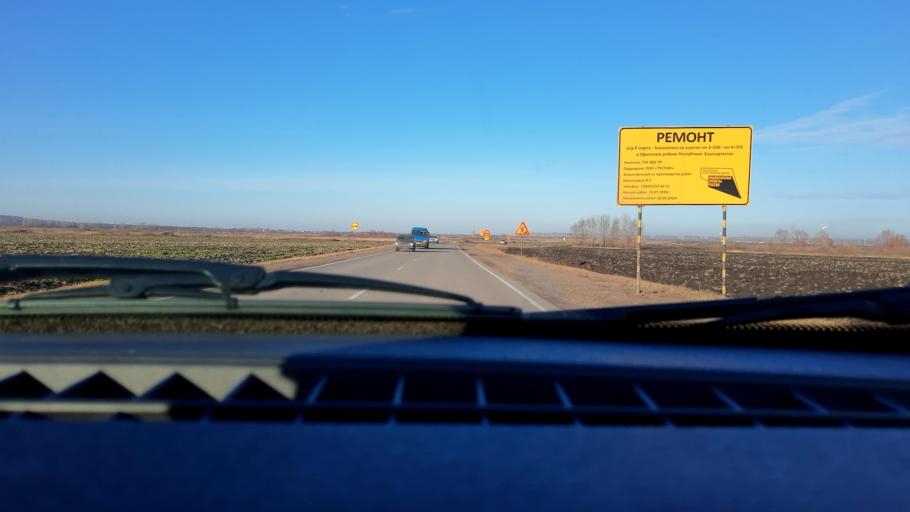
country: RU
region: Bashkortostan
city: Ufa
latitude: 54.8025
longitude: 55.9639
